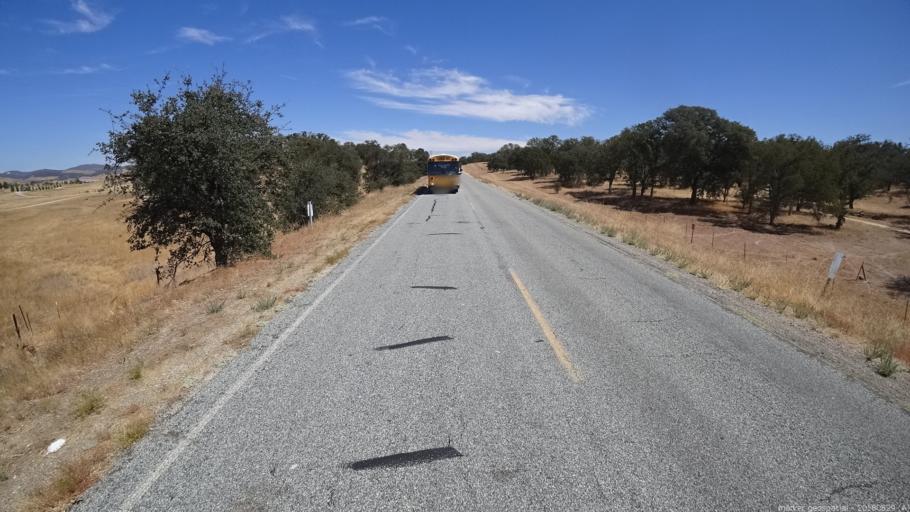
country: US
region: California
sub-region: Monterey County
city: King City
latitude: 35.9393
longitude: -121.1153
